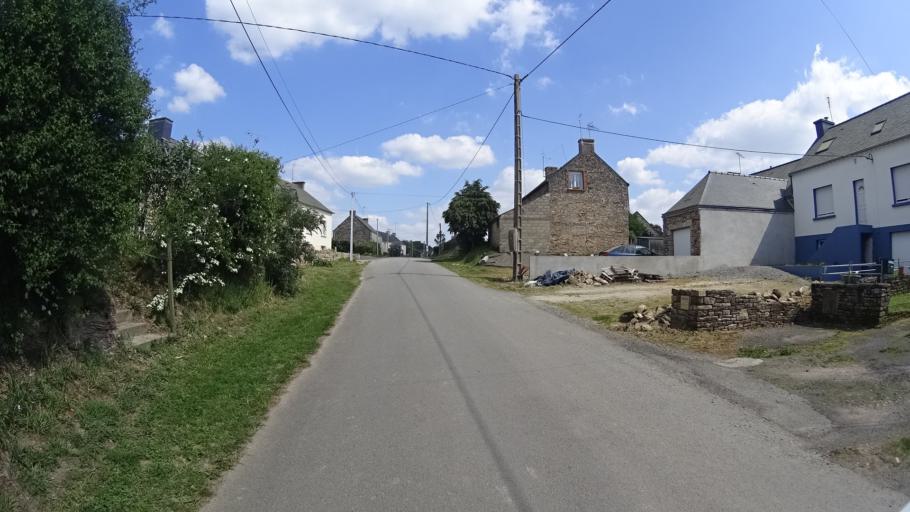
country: FR
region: Brittany
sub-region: Departement du Morbihan
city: Allaire
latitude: 47.6004
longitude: -2.1856
